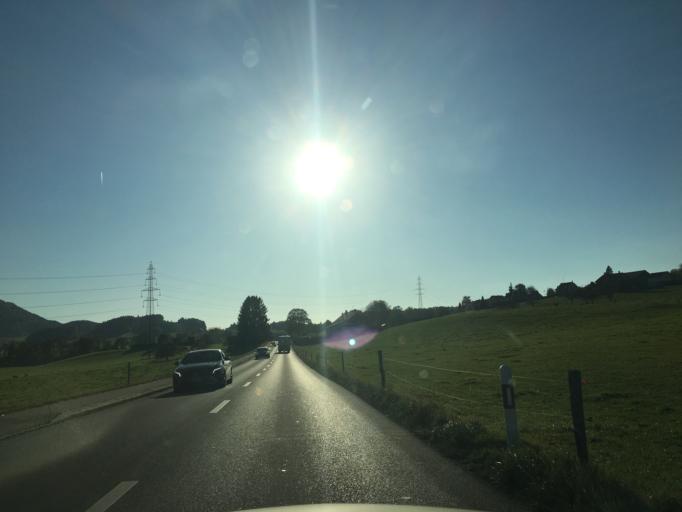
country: CH
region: Vaud
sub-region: Lavaux-Oron District
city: Savigny
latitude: 46.5388
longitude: 6.7657
